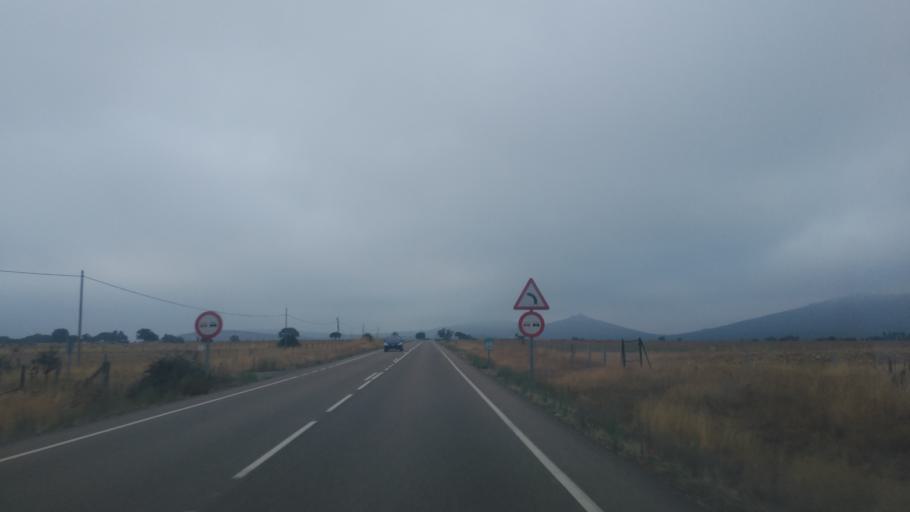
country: ES
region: Castille and Leon
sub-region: Provincia de Salamanca
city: Aldeanueva de la Sierra
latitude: 40.6300
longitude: -6.1082
